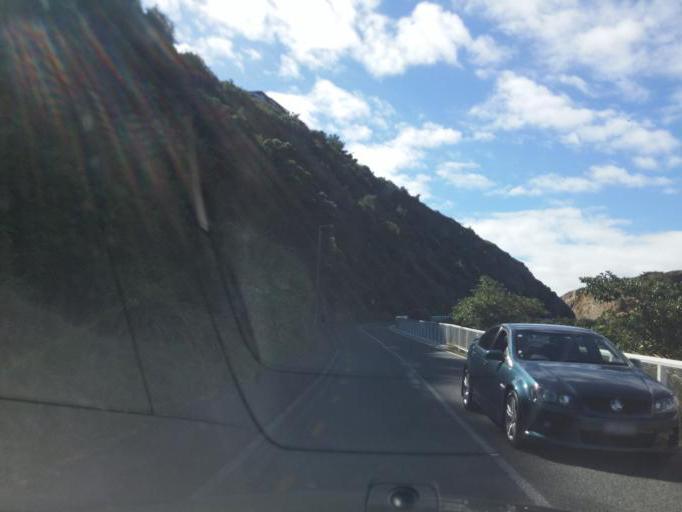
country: NZ
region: Wellington
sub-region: Wellington City
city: Wellington
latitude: -41.3312
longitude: 174.8303
